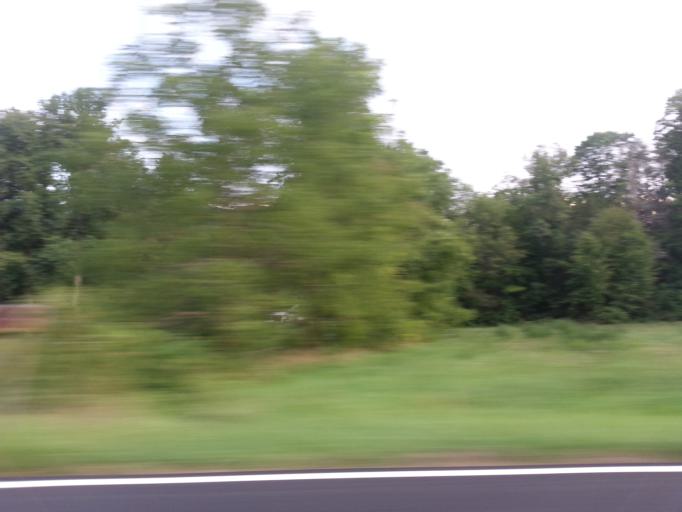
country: US
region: Tennessee
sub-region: Carter County
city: Hunter
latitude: 36.4628
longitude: -82.0114
